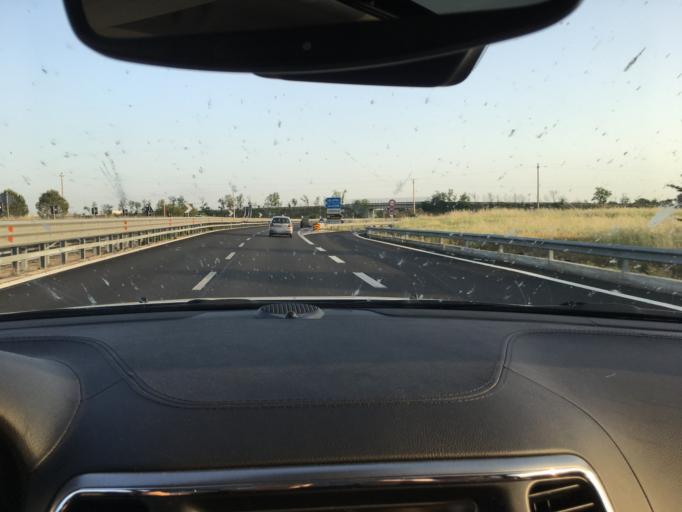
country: IT
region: Apulia
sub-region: Provincia di Lecce
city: Lequile
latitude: 40.2919
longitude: 18.1329
